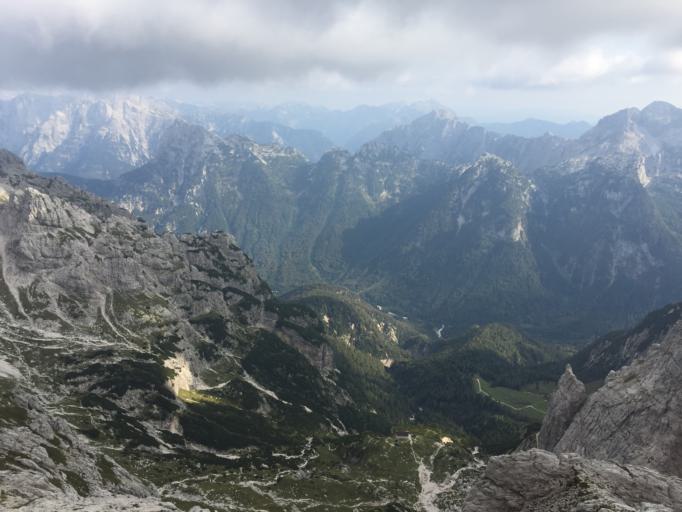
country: IT
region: Friuli Venezia Giulia
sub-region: Provincia di Udine
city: Malborghetto
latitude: 46.4279
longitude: 13.4938
